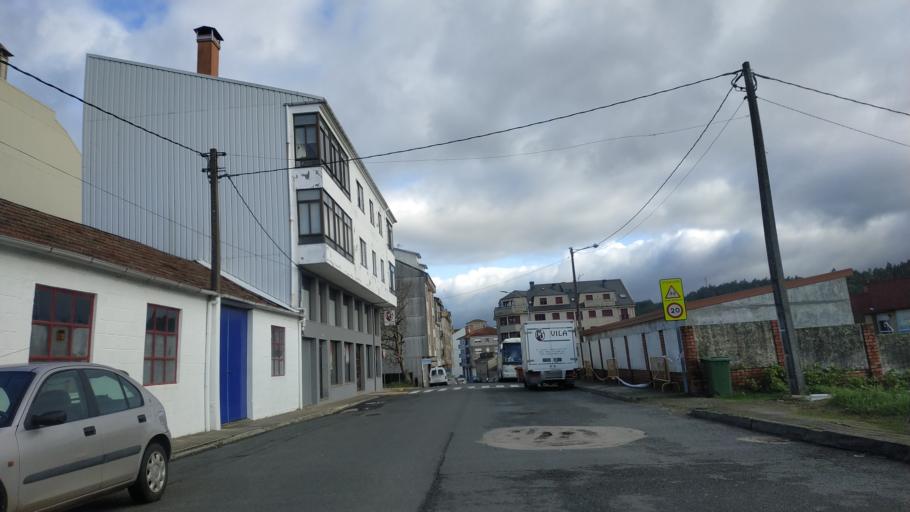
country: ES
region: Galicia
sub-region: Provincia de Pontevedra
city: Silleda
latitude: 42.7927
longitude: -8.1675
